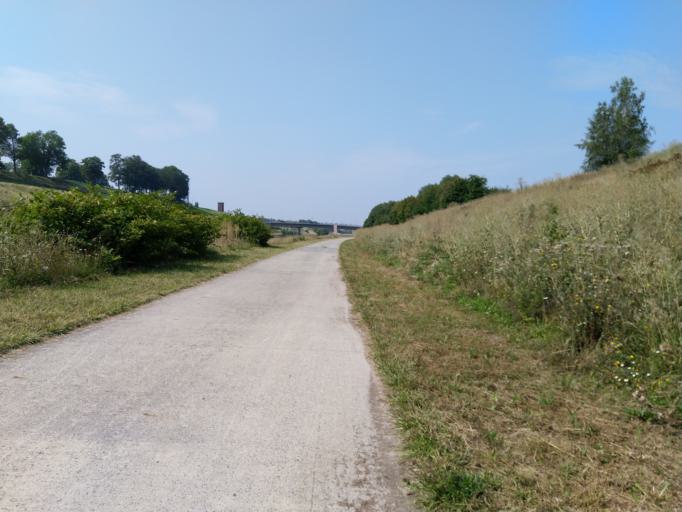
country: BE
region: Wallonia
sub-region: Province du Hainaut
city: Roeulx
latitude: 50.4736
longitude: 4.1000
